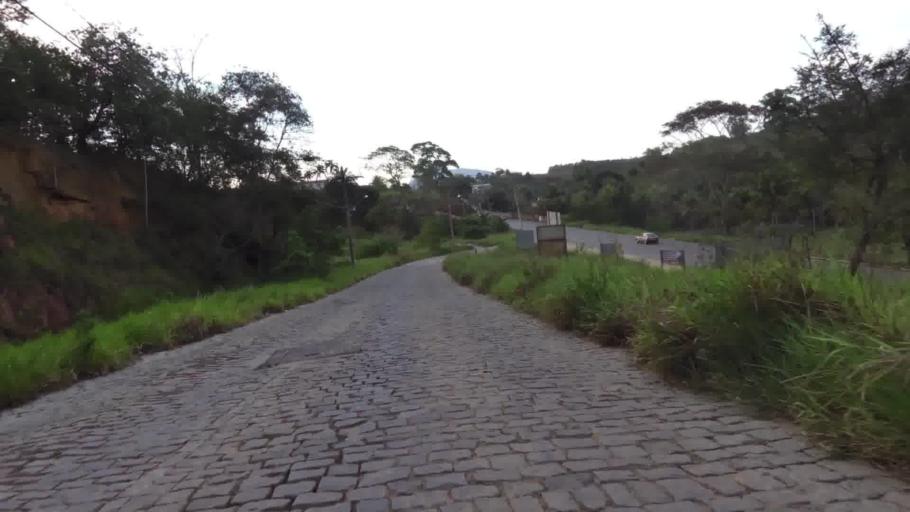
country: BR
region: Espirito Santo
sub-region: Piuma
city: Piuma
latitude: -20.8278
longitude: -40.7314
